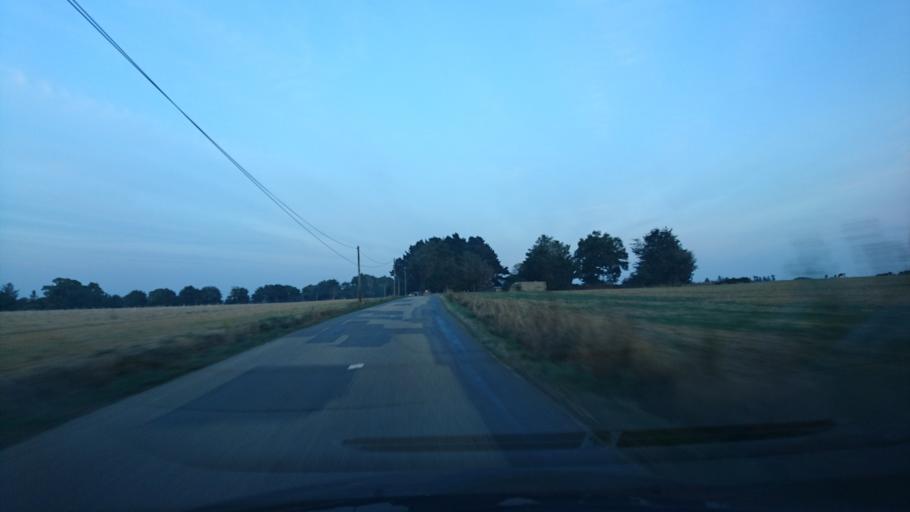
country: FR
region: Brittany
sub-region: Departement d'Ille-et-Vilaine
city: Guignen
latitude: 47.9136
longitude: -1.8768
